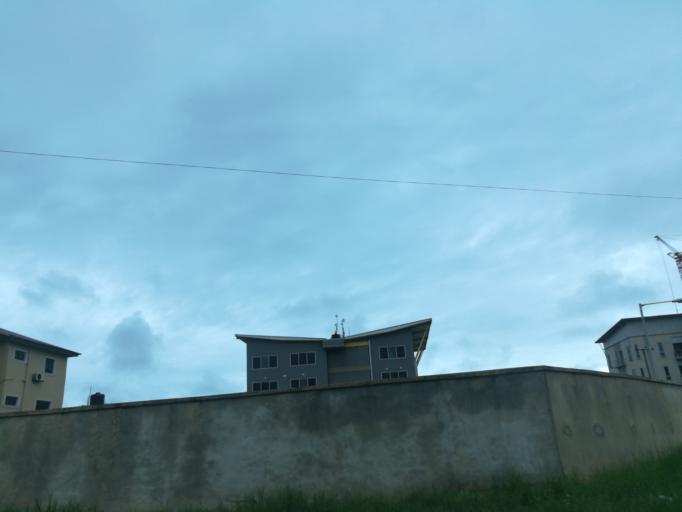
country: NG
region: Lagos
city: Ikoyi
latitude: 6.4397
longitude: 3.4731
